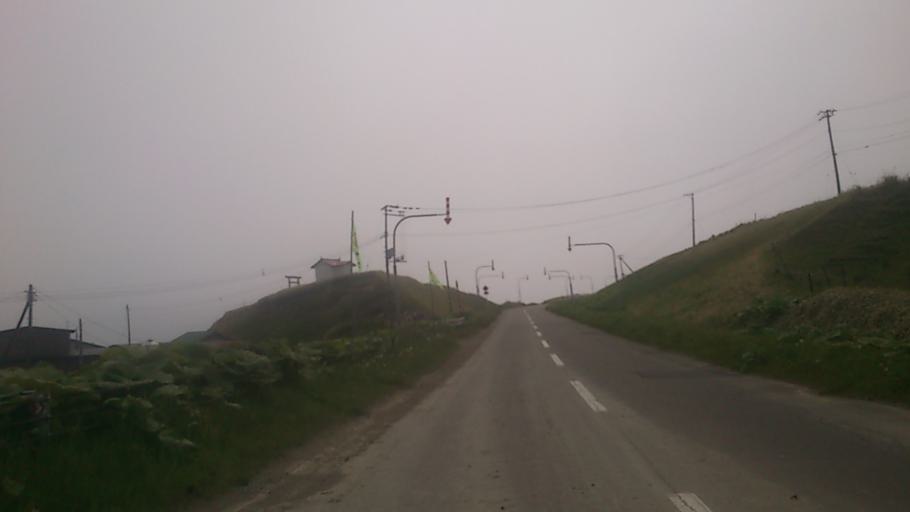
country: JP
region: Hokkaido
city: Nemuro
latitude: 43.1745
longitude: 145.2969
